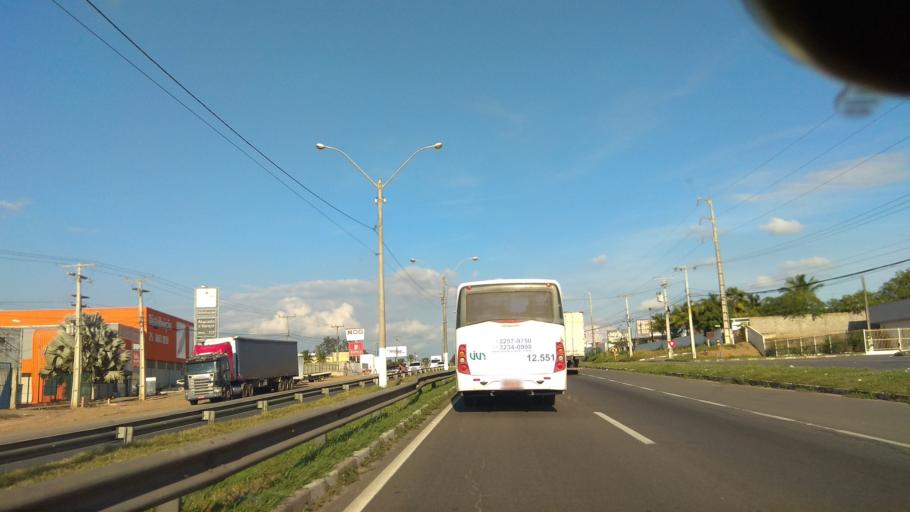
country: BR
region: Bahia
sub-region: Feira De Santana
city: Feira de Santana
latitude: -12.2919
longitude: -38.9095
